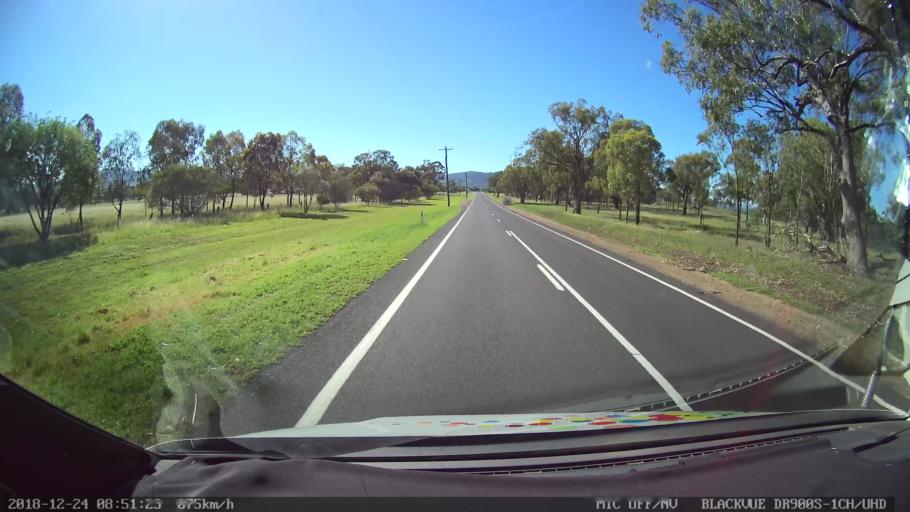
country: AU
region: New South Wales
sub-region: Liverpool Plains
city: Quirindi
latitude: -31.4840
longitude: 150.6736
